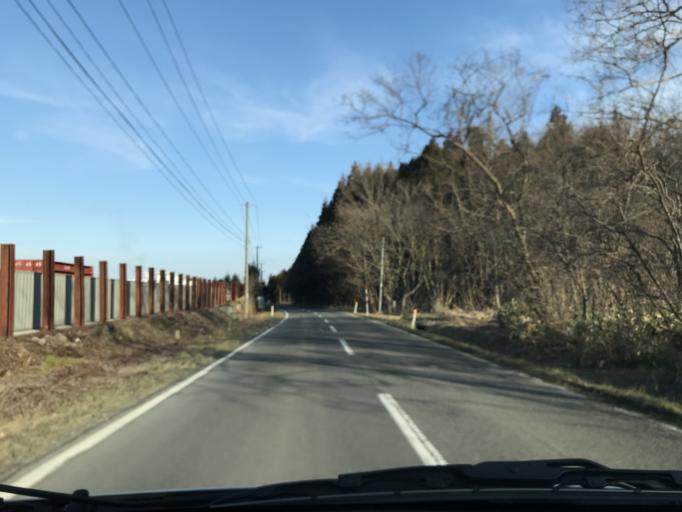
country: JP
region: Iwate
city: Kitakami
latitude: 39.2327
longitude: 141.0721
